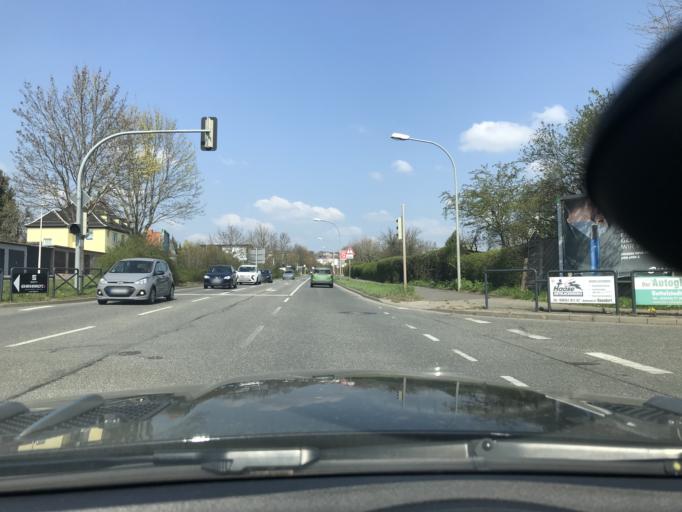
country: DE
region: Thuringia
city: Weimar
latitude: 50.9993
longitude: 11.3328
